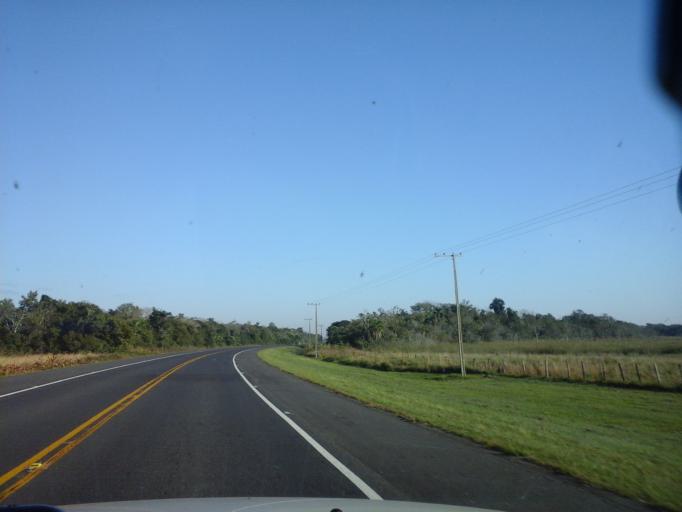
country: PY
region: Neembucu
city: Pilar
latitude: -26.8594
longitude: -57.9551
